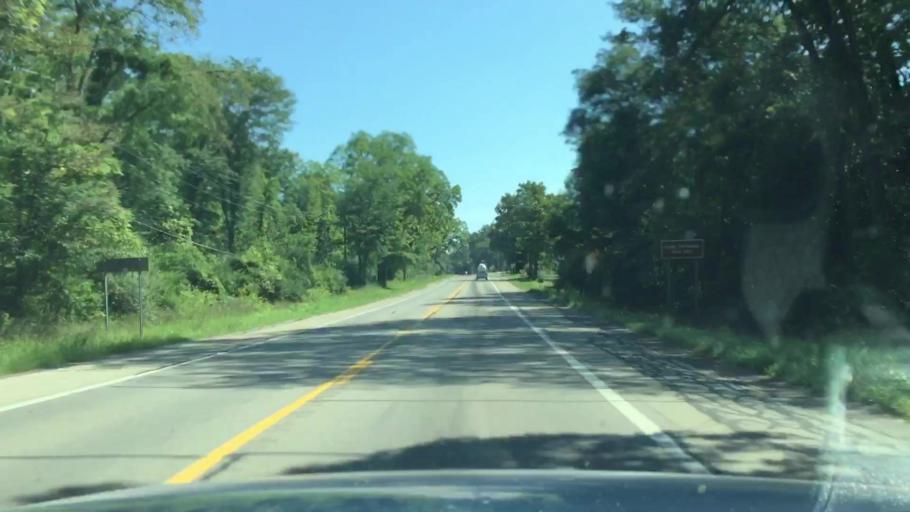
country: US
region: Michigan
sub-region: Jackson County
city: Brooklyn
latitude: 42.0567
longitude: -84.1453
